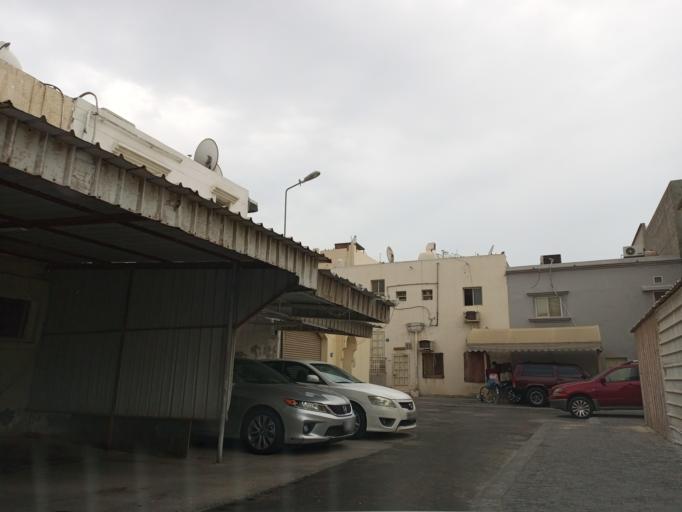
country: BH
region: Muharraq
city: Al Muharraq
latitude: 26.2585
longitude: 50.6347
